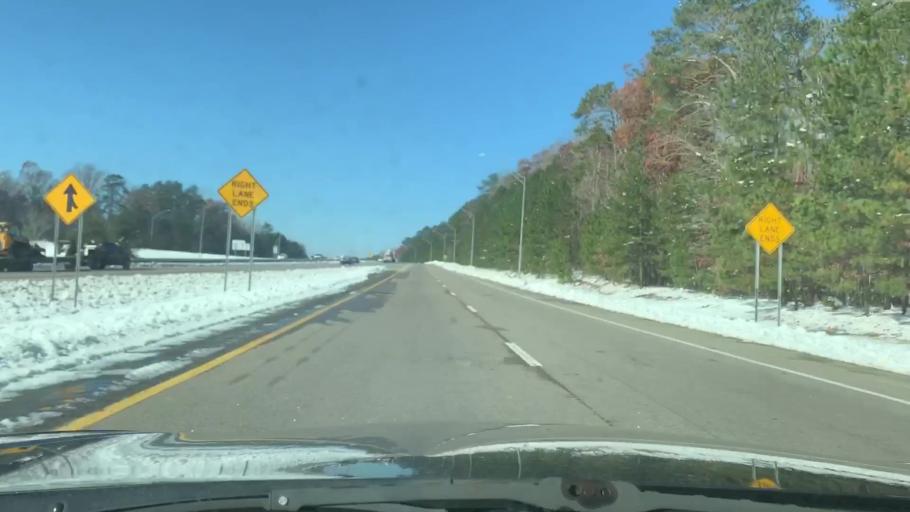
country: US
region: North Carolina
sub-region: Durham County
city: Durham
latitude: 36.0342
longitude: -78.9657
